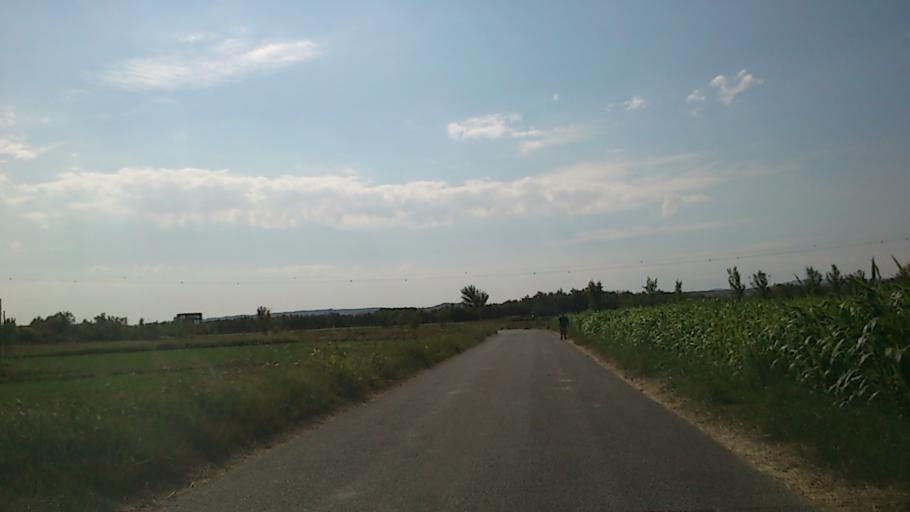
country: ES
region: Aragon
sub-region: Provincia de Zaragoza
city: Puebla de Alfinden
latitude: 41.6111
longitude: -0.7599
